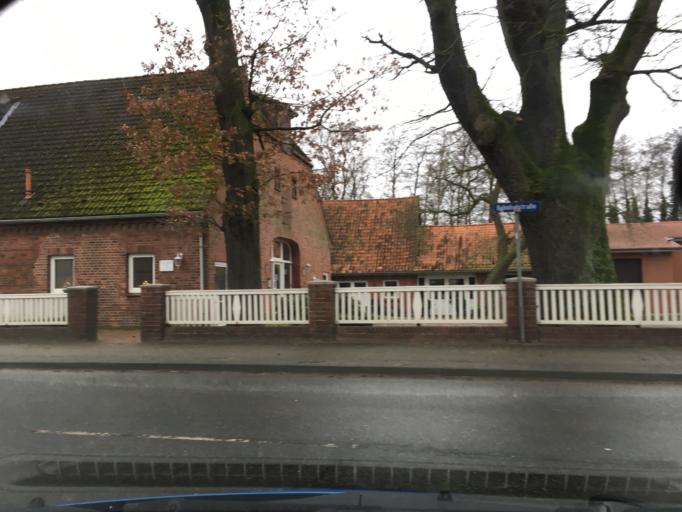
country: DE
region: Lower Saxony
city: Neetze
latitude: 53.2685
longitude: 10.6253
